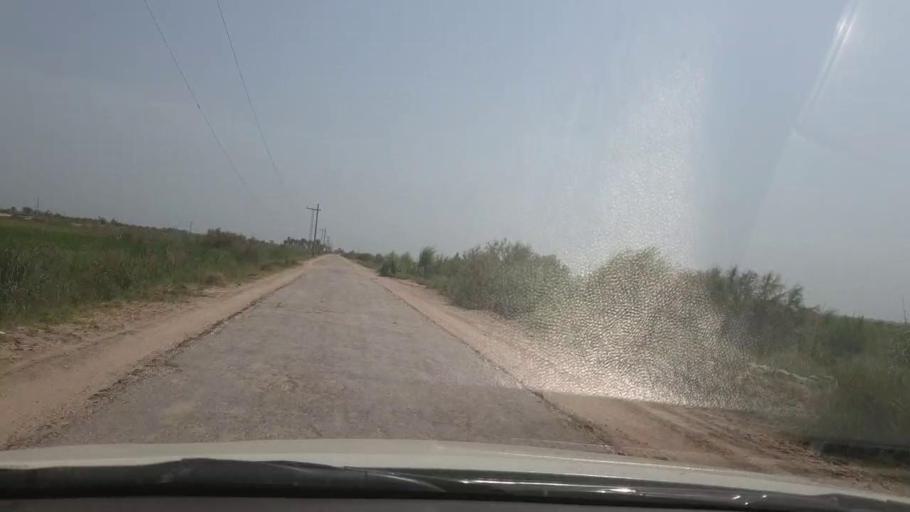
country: PK
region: Sindh
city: Garhi Yasin
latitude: 27.9638
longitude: 68.5045
